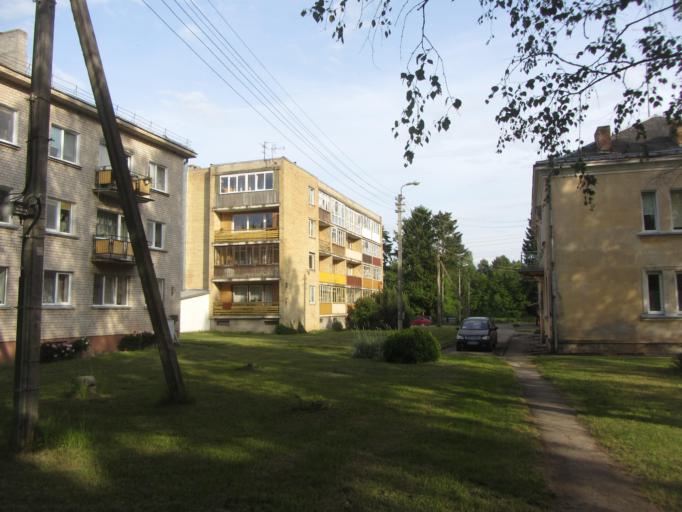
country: LT
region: Panevezys
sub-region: Birzai
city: Birzai
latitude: 56.1977
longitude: 24.6261
